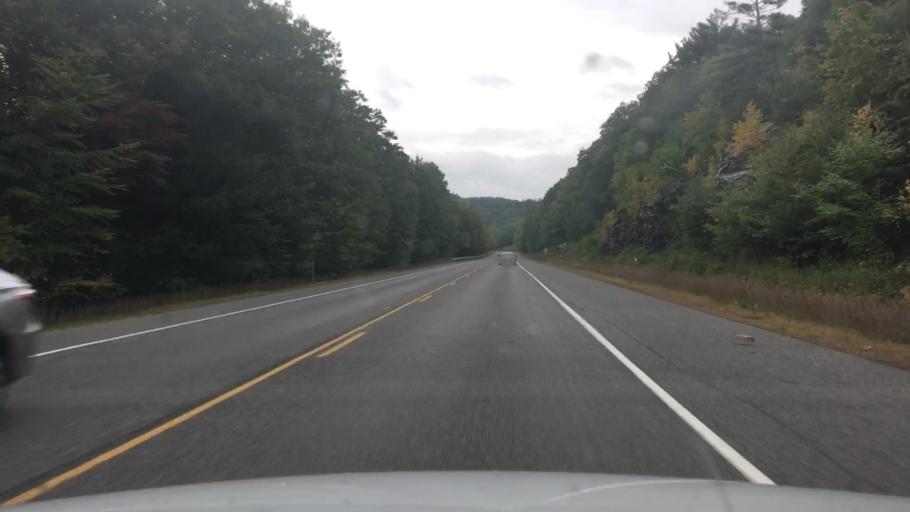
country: US
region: New Hampshire
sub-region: Carroll County
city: Wolfeboro
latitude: 43.5278
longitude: -71.2744
